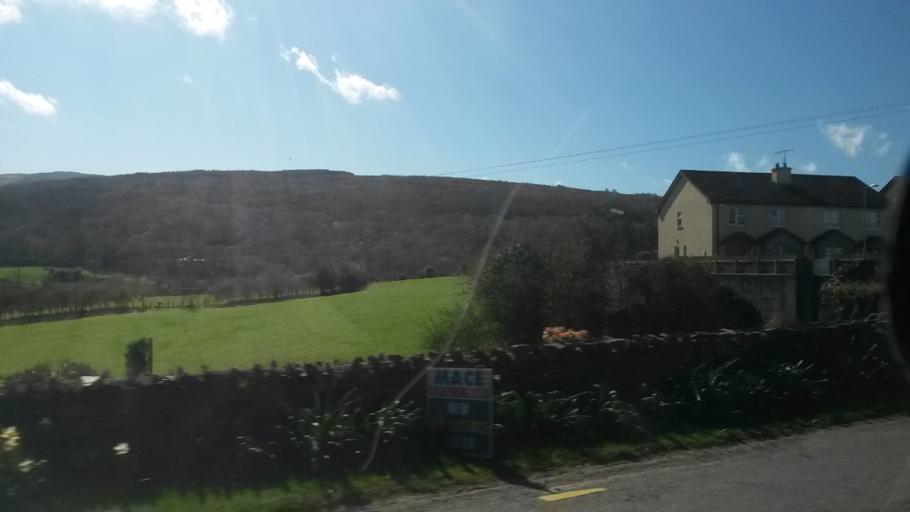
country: IE
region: Munster
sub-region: Ciarrai
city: Kenmare
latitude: 51.9046
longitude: -9.4349
